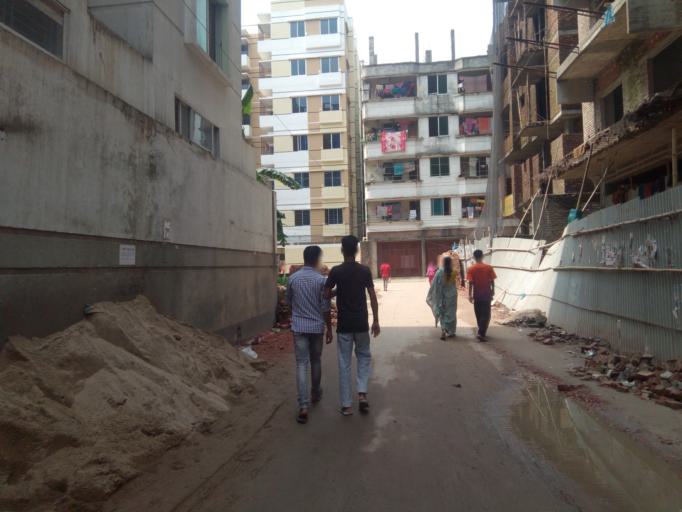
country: BD
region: Dhaka
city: Paltan
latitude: 23.7611
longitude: 90.4401
